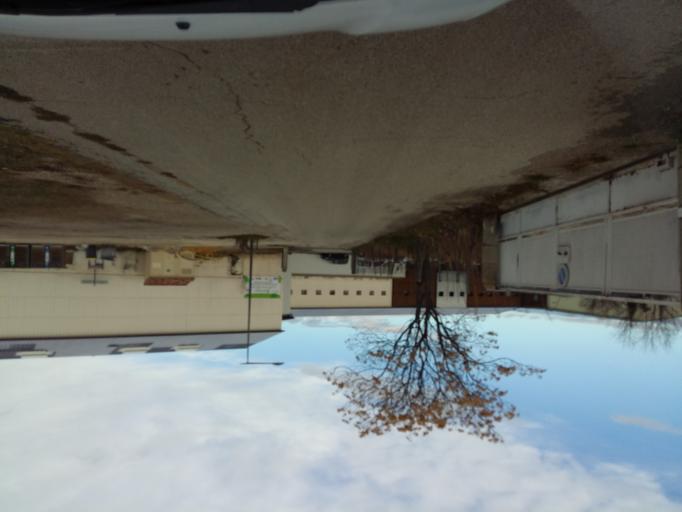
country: FR
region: Provence-Alpes-Cote d'Azur
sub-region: Departement du Vaucluse
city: Valreas
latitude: 44.3850
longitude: 4.9850
